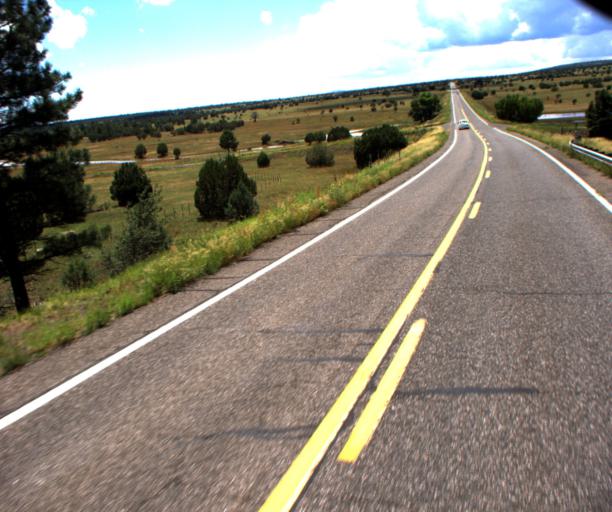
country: US
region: Arizona
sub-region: Gila County
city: Pine
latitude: 34.5043
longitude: -111.5753
